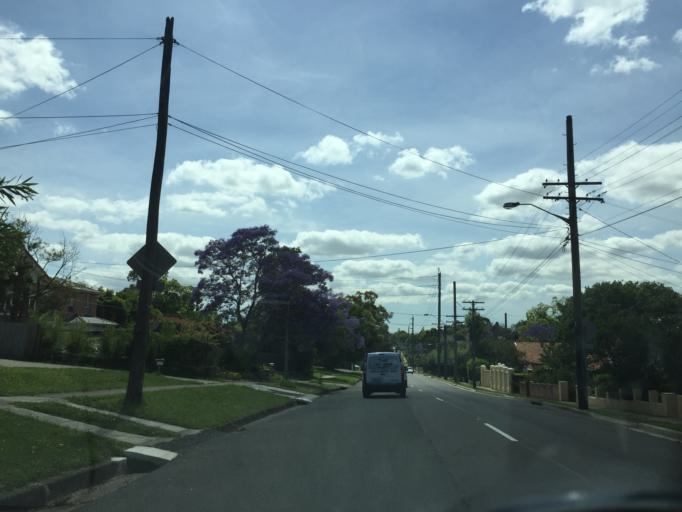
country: AU
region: New South Wales
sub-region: Ryde
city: West Ryde
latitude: -33.7952
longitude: 151.0709
